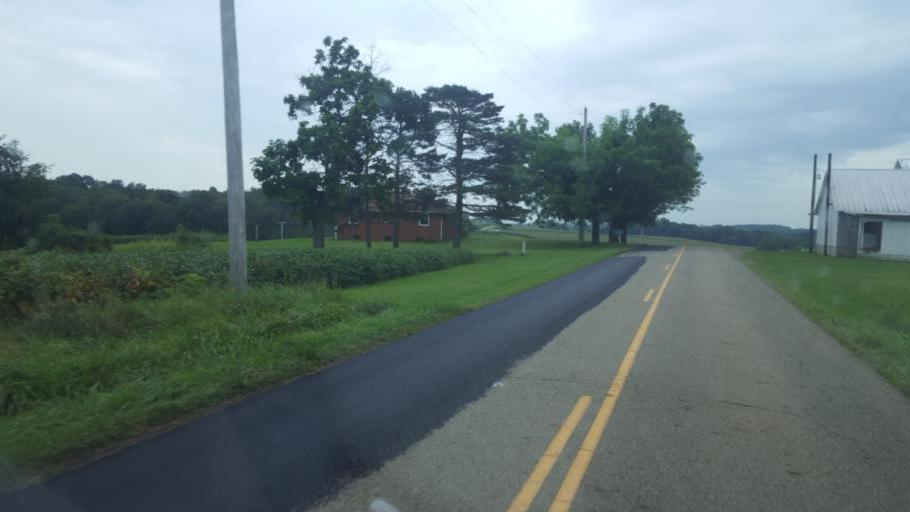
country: US
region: Ohio
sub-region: Knox County
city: Gambier
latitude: 40.4869
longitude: -82.3831
